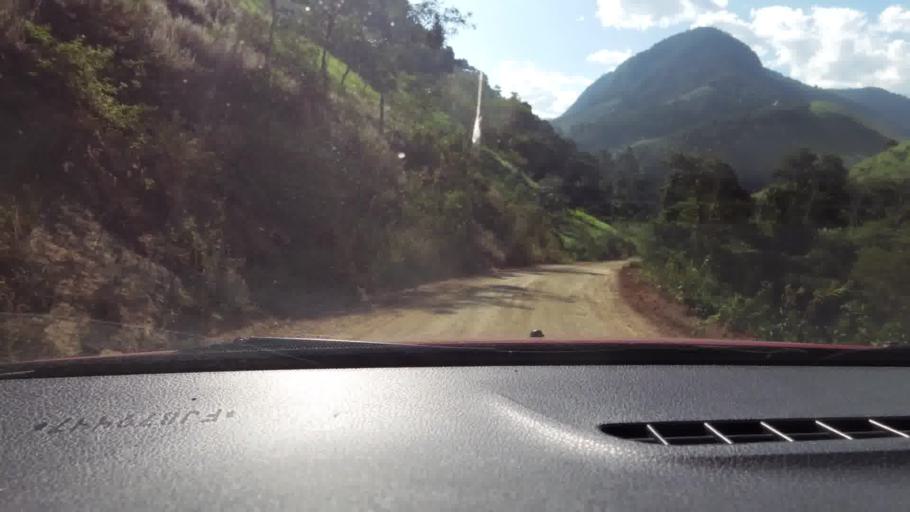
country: BR
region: Espirito Santo
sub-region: Guarapari
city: Guarapari
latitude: -20.5276
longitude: -40.5645
